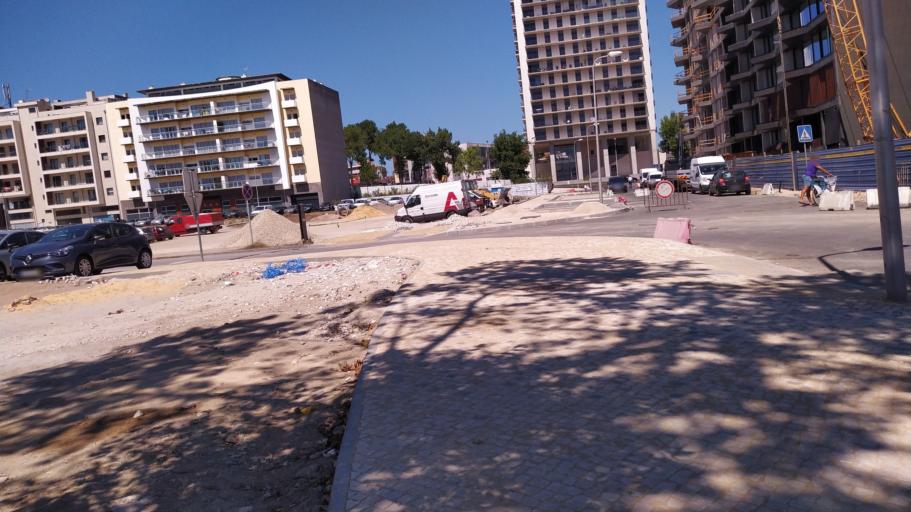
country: PT
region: Aveiro
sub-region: Aveiro
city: Aveiro
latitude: 40.6399
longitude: -8.6434
